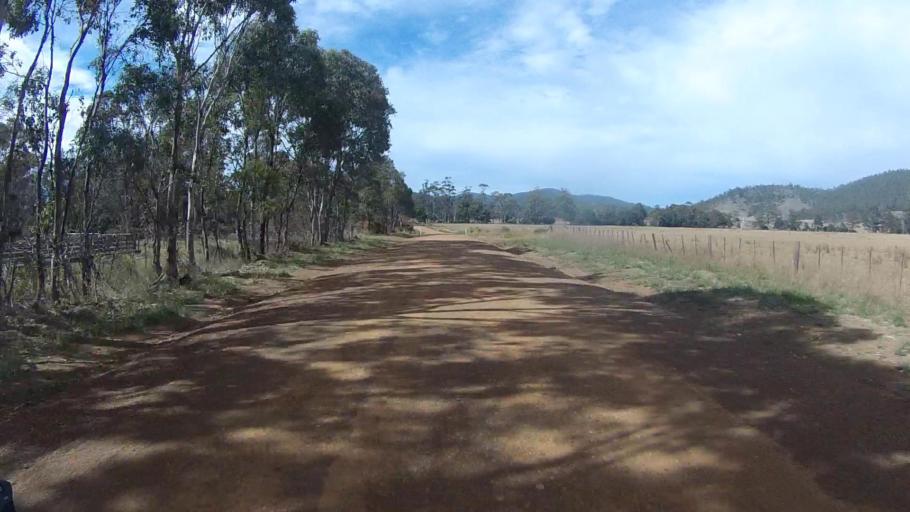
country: AU
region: Tasmania
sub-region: Sorell
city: Sorell
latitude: -42.6378
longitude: 147.9003
